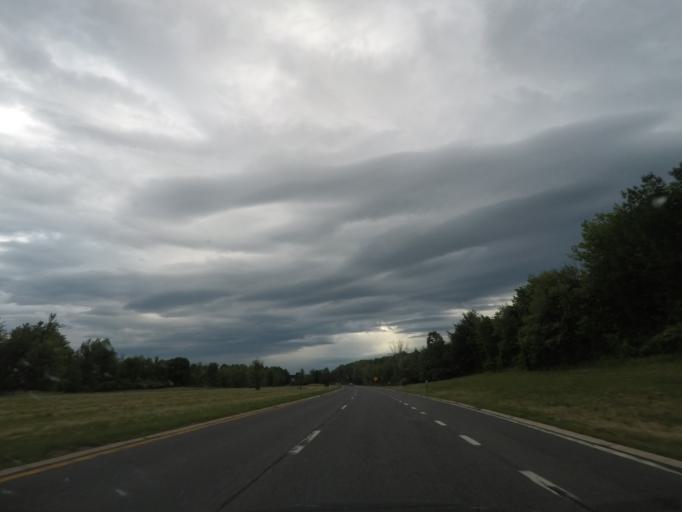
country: US
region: New York
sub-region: Dutchess County
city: Pine Plains
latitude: 42.0962
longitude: -73.7193
